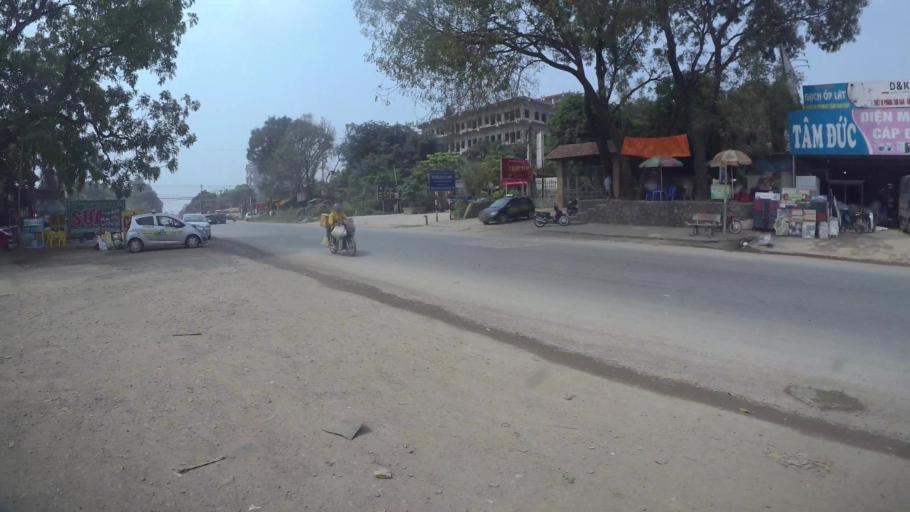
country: VN
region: Ha Noi
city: Lien Quan
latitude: 20.9846
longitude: 105.5264
